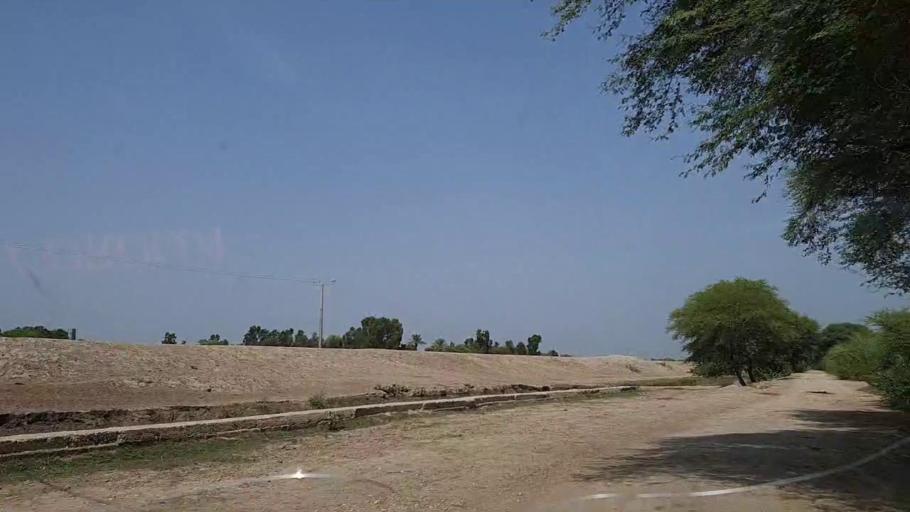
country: PK
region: Sindh
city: Ghotki
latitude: 28.0727
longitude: 69.3180
